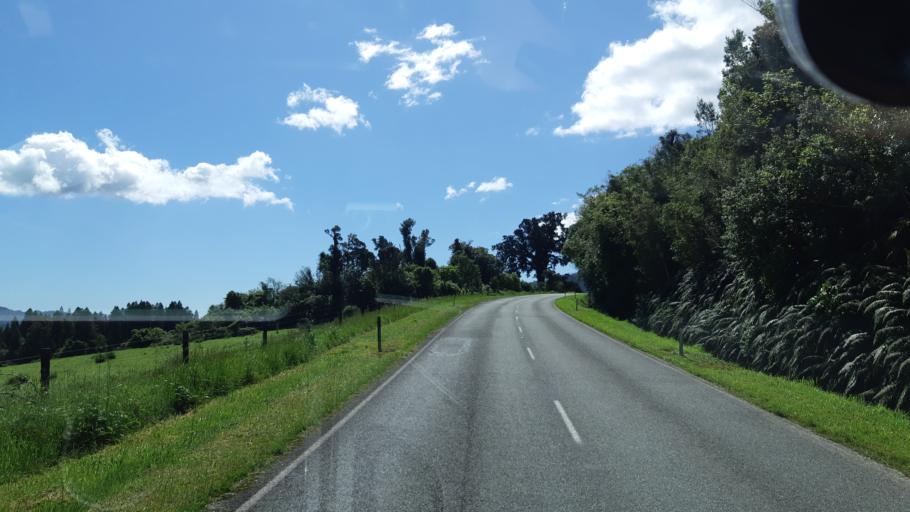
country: NZ
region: West Coast
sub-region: Westland District
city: Hokitika
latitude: -43.0909
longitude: 170.6280
